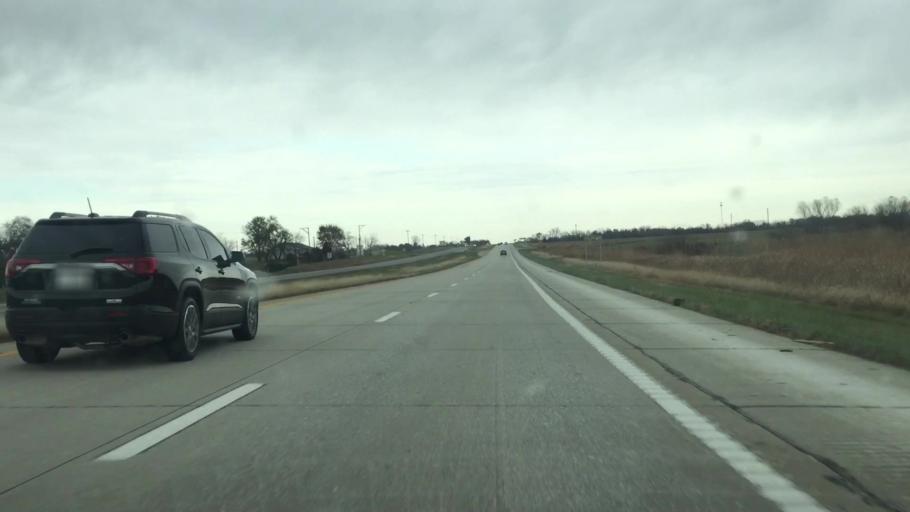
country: US
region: Missouri
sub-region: Saint Clair County
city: Osceola
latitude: 38.1483
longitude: -93.7229
